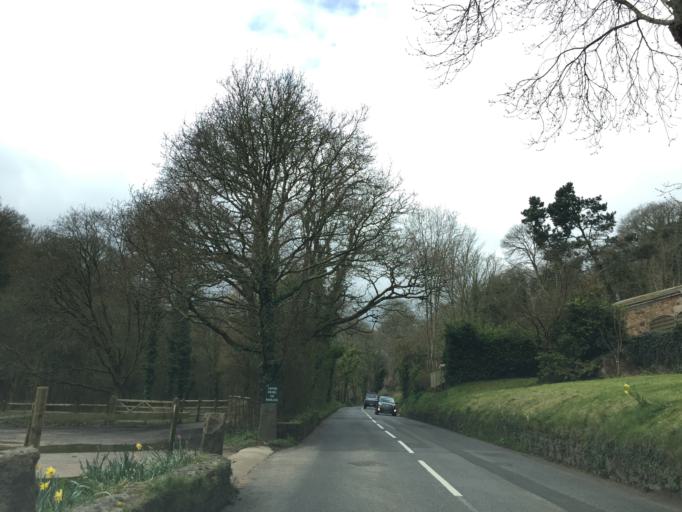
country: JE
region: St Helier
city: Saint Helier
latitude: 49.2122
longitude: -2.1646
